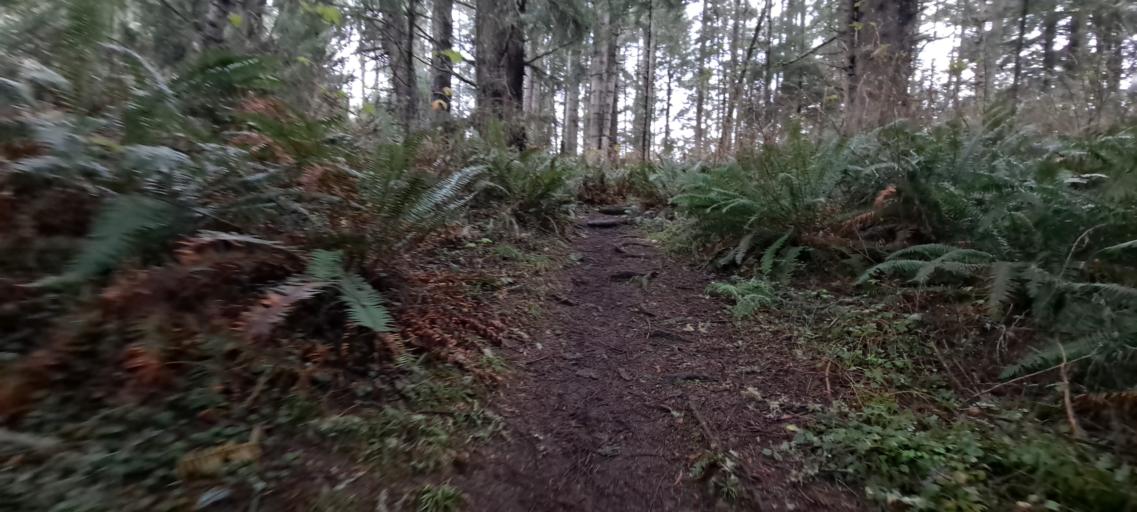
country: US
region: California
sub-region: Humboldt County
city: Ferndale
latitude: 40.5672
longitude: -124.2556
